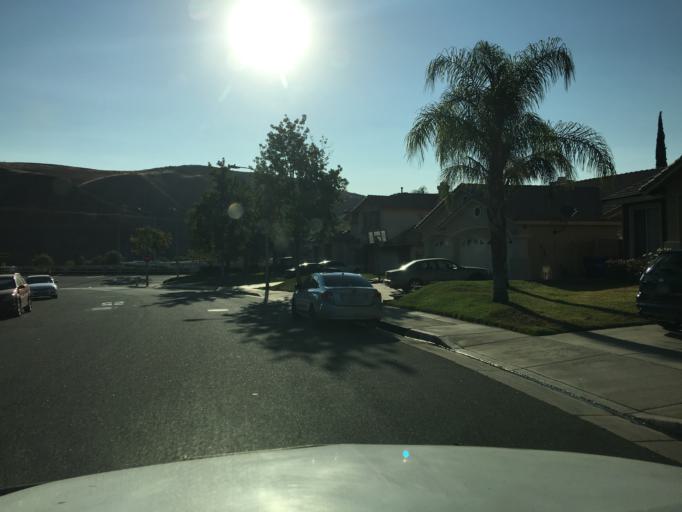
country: US
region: California
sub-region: Los Angeles County
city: Castaic
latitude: 34.5075
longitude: -118.6341
